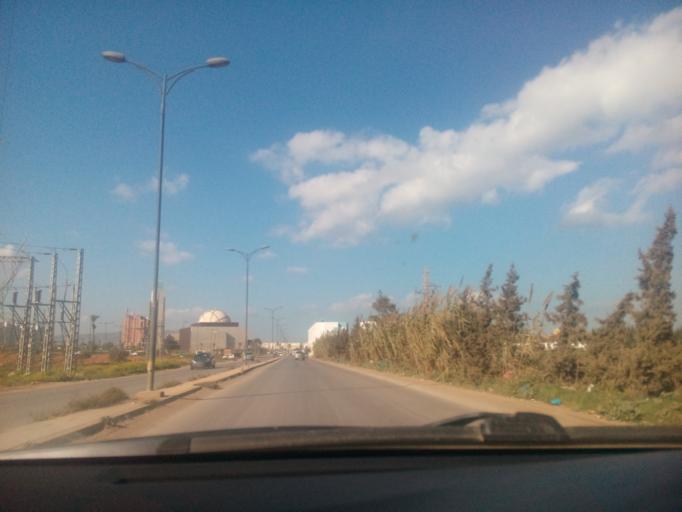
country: DZ
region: Oran
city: Es Senia
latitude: 35.6774
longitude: -0.5976
